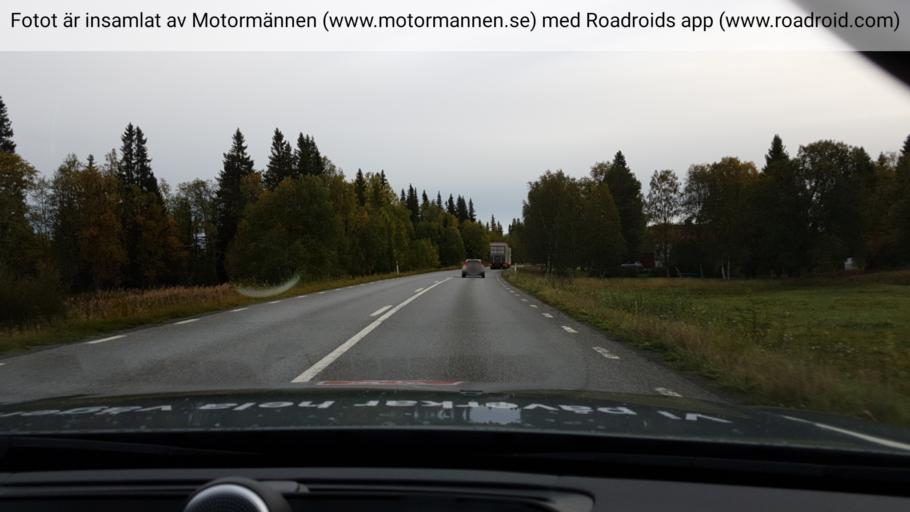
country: SE
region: Jaemtland
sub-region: OEstersunds Kommun
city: Lit
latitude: 63.4354
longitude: 15.1233
